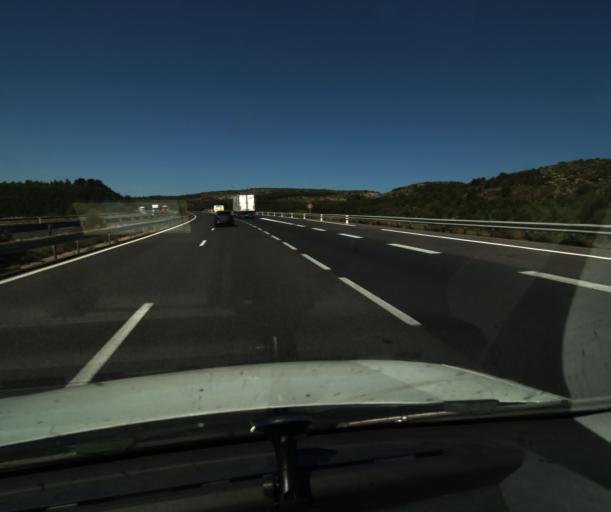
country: FR
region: Languedoc-Roussillon
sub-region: Departement des Pyrenees-Orientales
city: Salses-le-Chateau
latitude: 42.8451
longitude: 2.9179
